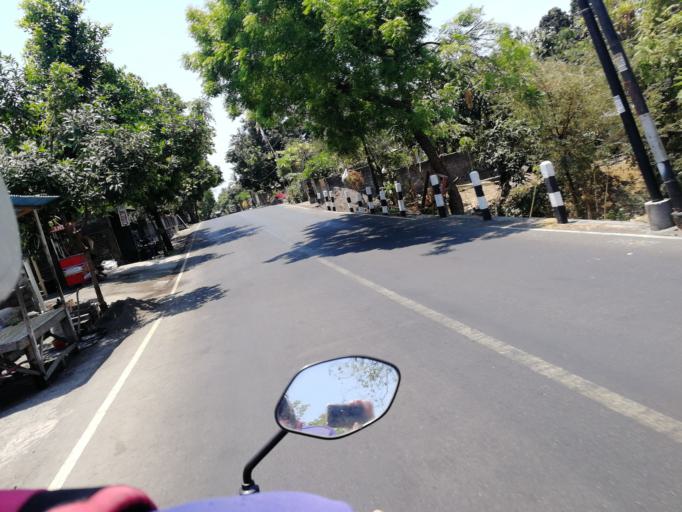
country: ID
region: Bali
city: Banjar Trunyan
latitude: -8.1510
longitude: 115.4117
